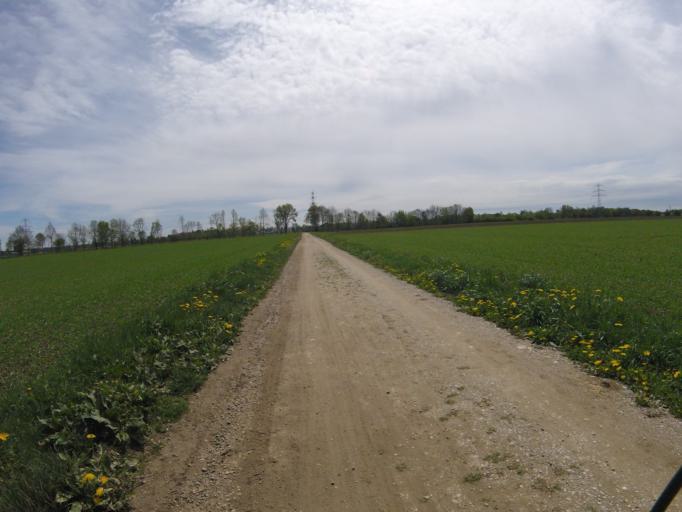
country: DE
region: Bavaria
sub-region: Upper Bavaria
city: Hohenbrunn
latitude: 48.0565
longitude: 11.6926
